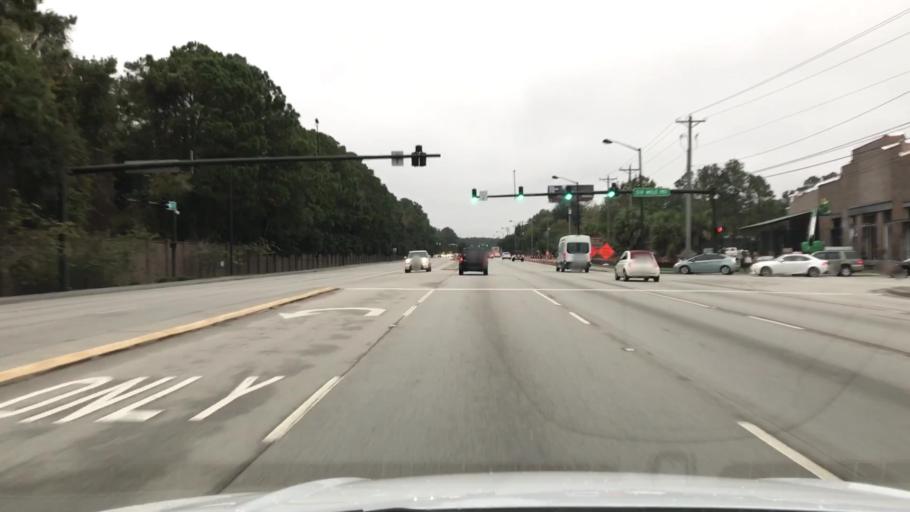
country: US
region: South Carolina
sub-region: Charleston County
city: Isle of Palms
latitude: 32.8414
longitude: -79.8173
